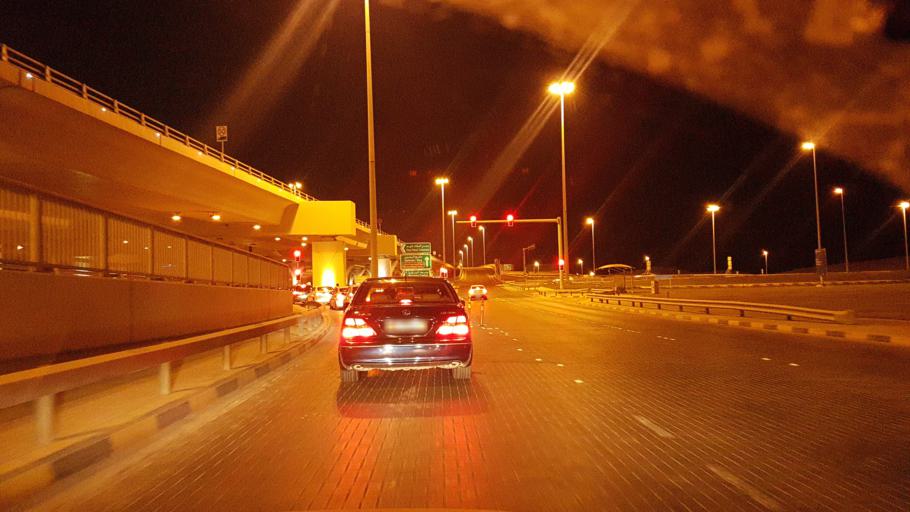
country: BH
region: Muharraq
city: Al Muharraq
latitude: 26.2460
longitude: 50.5909
